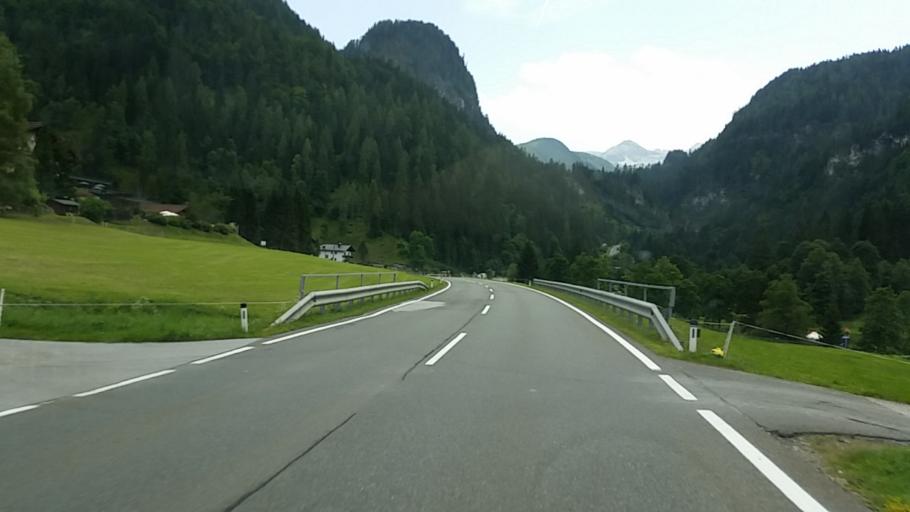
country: AT
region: Salzburg
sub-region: Politischer Bezirk Sankt Johann im Pongau
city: Untertauern
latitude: 47.3039
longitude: 13.5057
